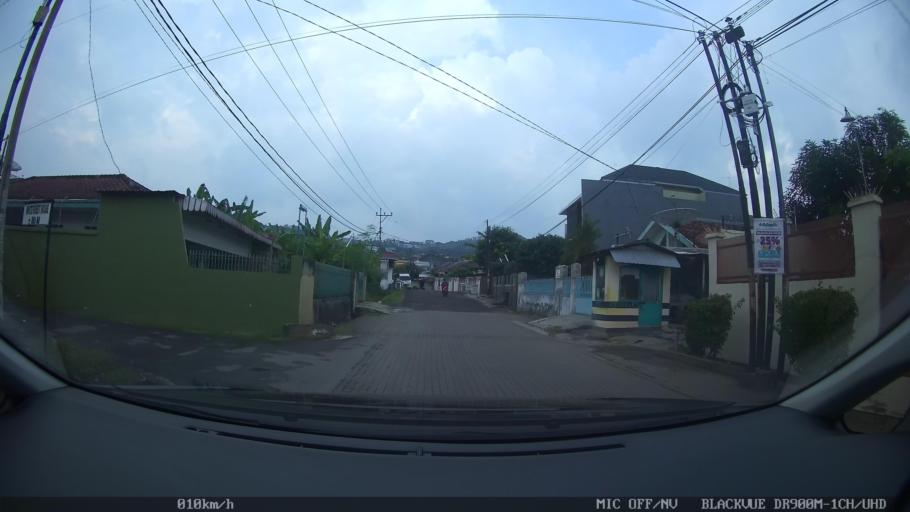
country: ID
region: Lampung
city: Bandarlampung
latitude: -5.4406
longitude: 105.2803
